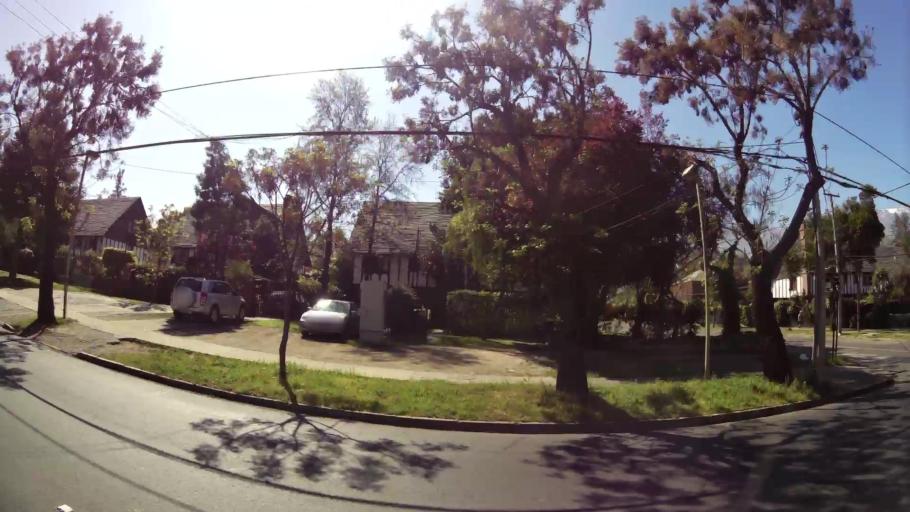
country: CL
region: Santiago Metropolitan
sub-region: Provincia de Santiago
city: Villa Presidente Frei, Nunoa, Santiago, Chile
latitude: -33.4094
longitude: -70.5365
